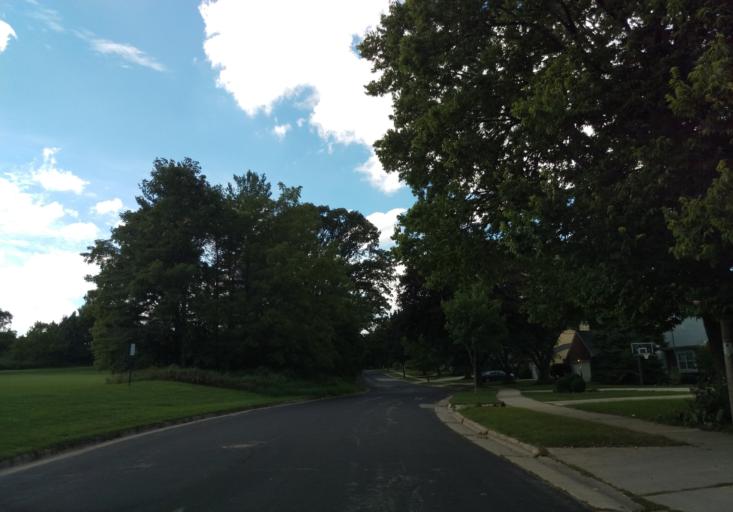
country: US
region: Wisconsin
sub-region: Dane County
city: Shorewood Hills
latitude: 43.0645
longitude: -89.4733
